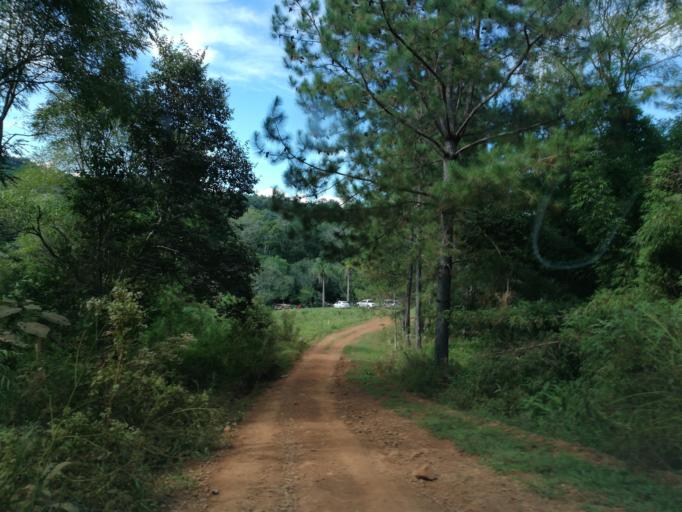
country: AR
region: Misiones
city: Dos de Mayo
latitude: -27.0159
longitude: -54.4159
